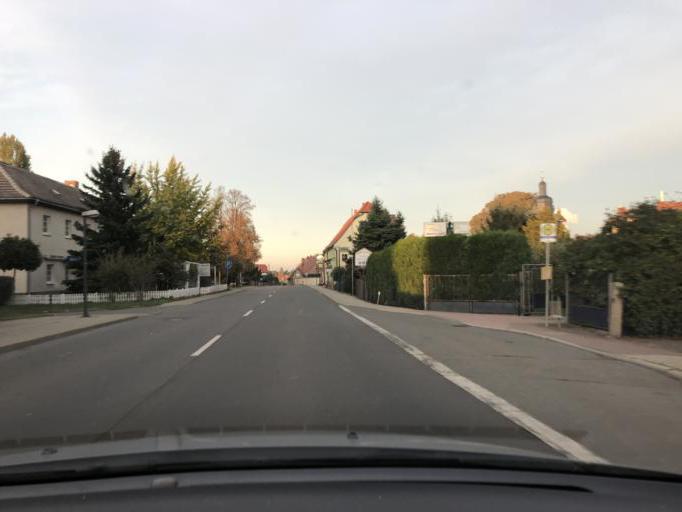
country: DE
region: Saxony
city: Elstertrebnitz
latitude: 51.1108
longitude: 12.1933
